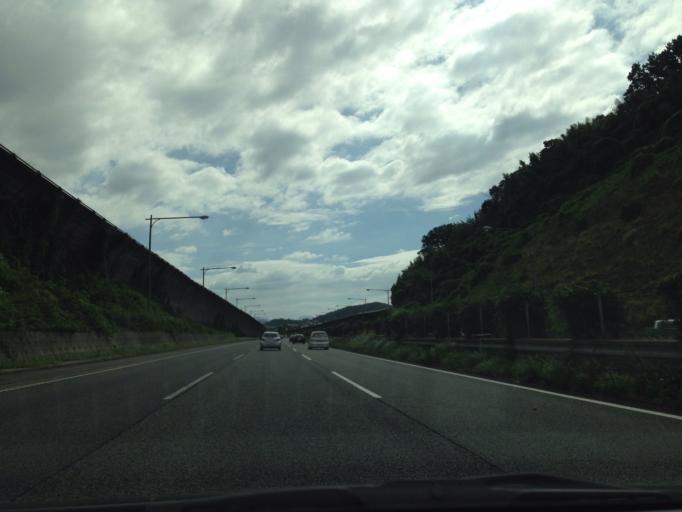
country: JP
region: Kanagawa
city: Isehara
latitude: 35.3857
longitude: 139.2760
